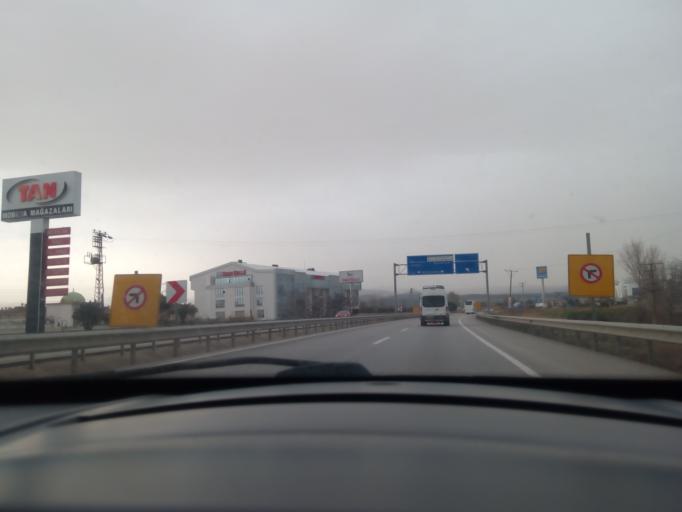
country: TR
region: Bursa
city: Tatkavakli
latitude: 40.0373
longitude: 28.3765
